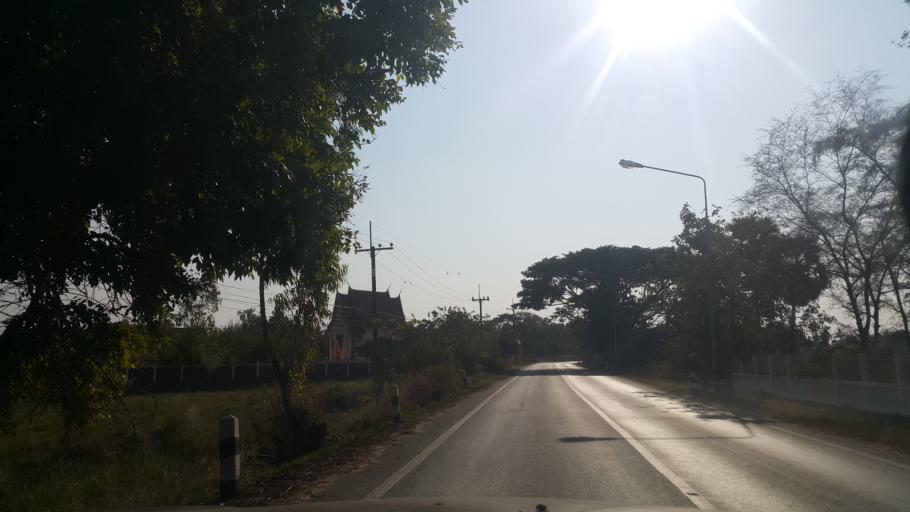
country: TH
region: Nakhon Ratchasima
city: Phimai
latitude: 15.1675
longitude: 102.3931
